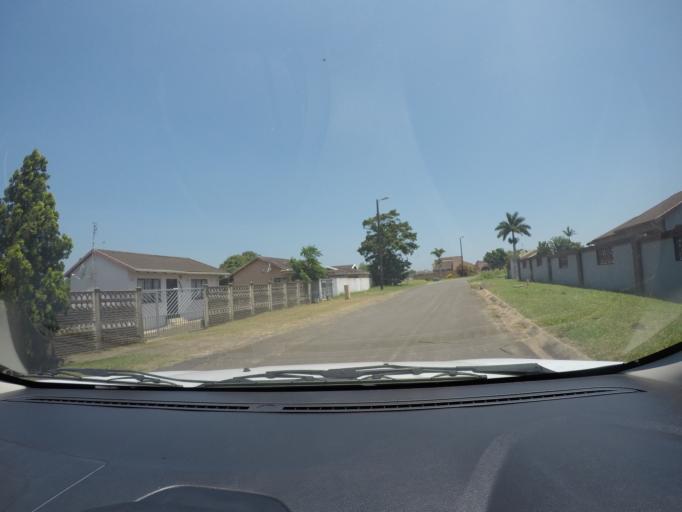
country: ZA
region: KwaZulu-Natal
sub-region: uThungulu District Municipality
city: eSikhawini
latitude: -28.8868
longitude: 31.8858
